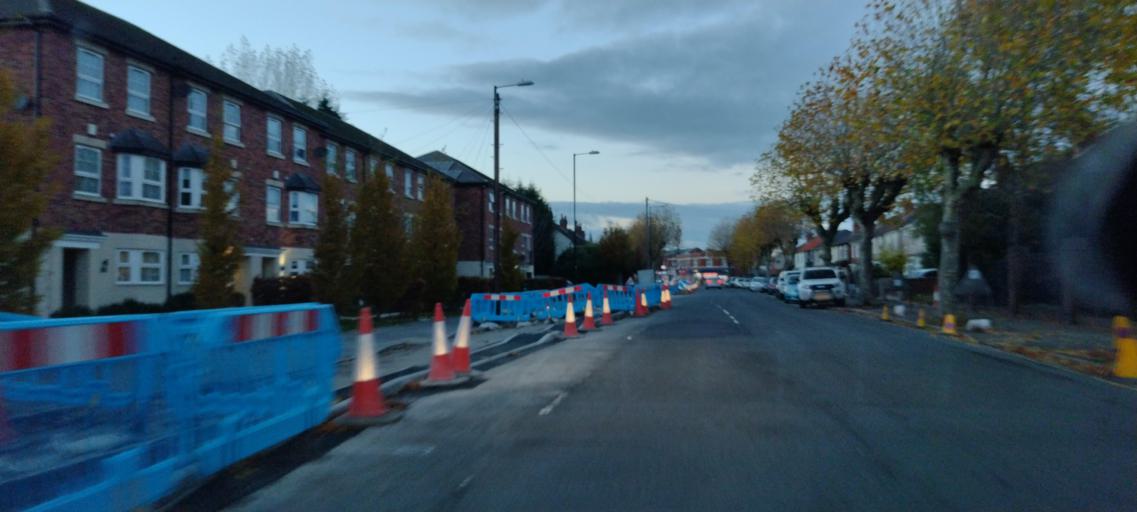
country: GB
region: England
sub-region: Coventry
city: Coventry
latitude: 52.4151
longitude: -1.5241
